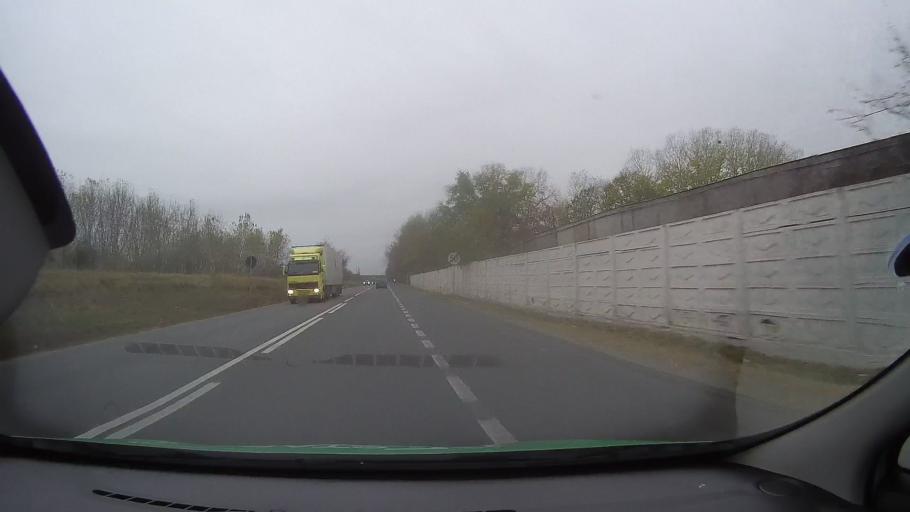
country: RO
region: Ialomita
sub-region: Comuna Slobozia
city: Slobozia
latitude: 44.5599
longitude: 27.3735
